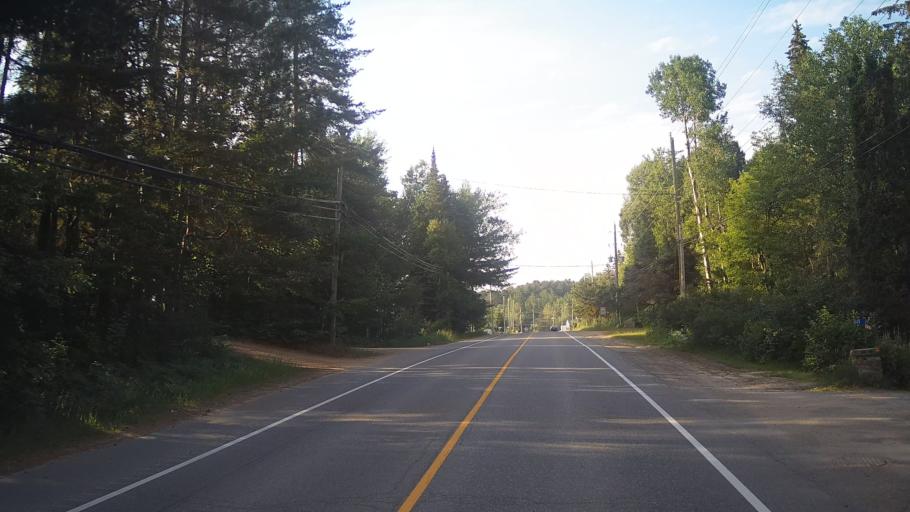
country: CA
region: Ontario
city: Huntsville
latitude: 45.3485
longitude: -79.2014
